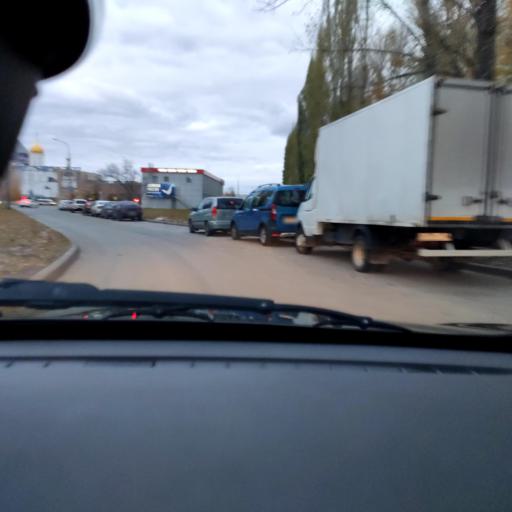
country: RU
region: Samara
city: Tol'yatti
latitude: 53.5267
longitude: 49.2821
